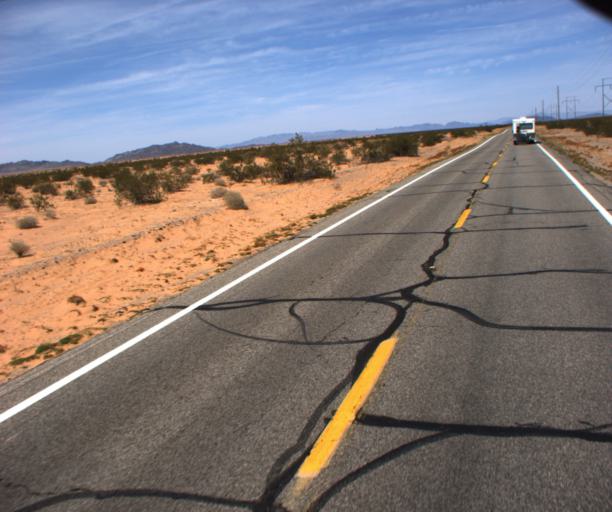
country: US
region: Arizona
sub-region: La Paz County
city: Quartzsite
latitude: 33.8984
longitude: -114.2169
